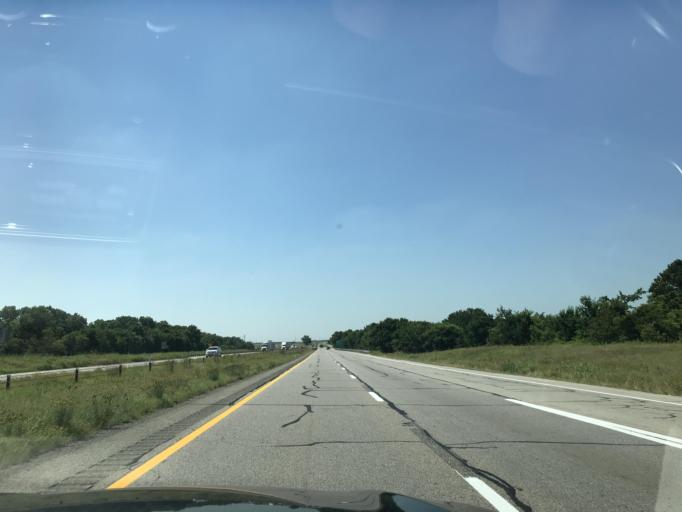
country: US
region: Texas
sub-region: Johnson County
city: Grandview
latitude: 32.2957
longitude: -97.1801
